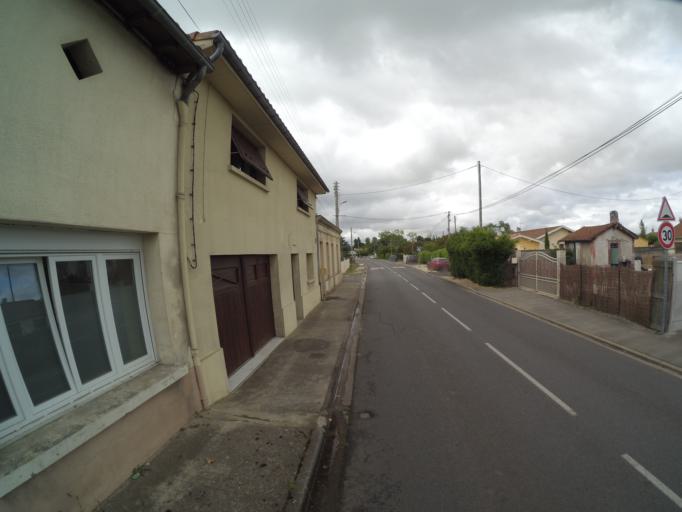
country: FR
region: Aquitaine
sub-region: Departement de la Gironde
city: Macau
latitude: 45.0090
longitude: -0.6158
